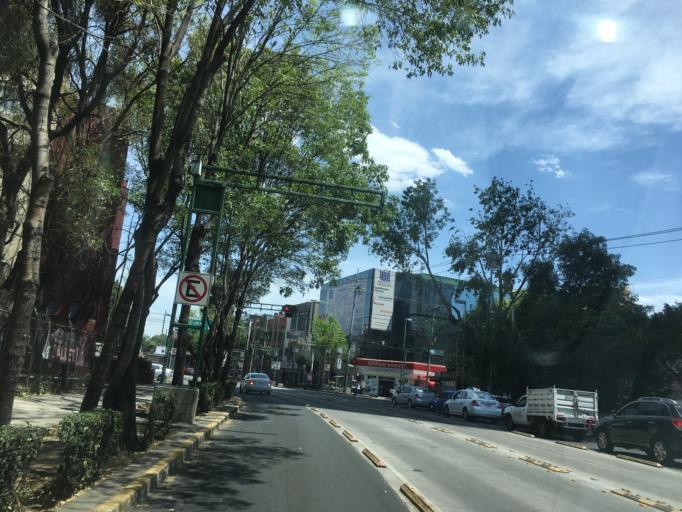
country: MX
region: Mexico City
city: Benito Juarez
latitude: 19.3974
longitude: -99.1652
